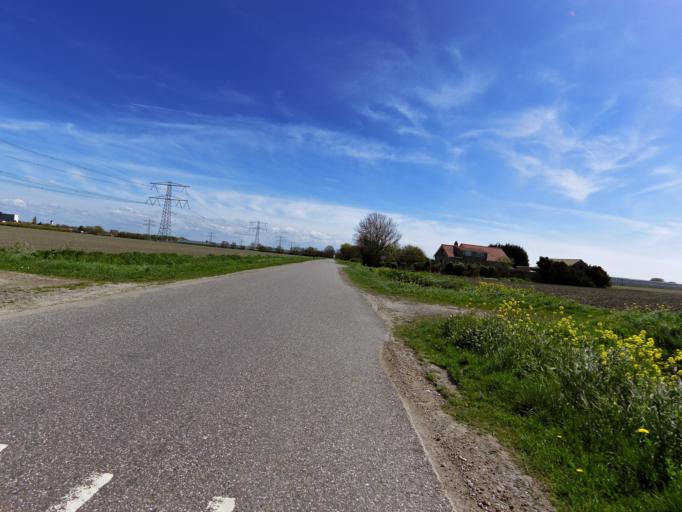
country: NL
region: South Holland
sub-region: Gemeente Brielle
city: Brielle
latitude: 51.9015
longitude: 4.1362
